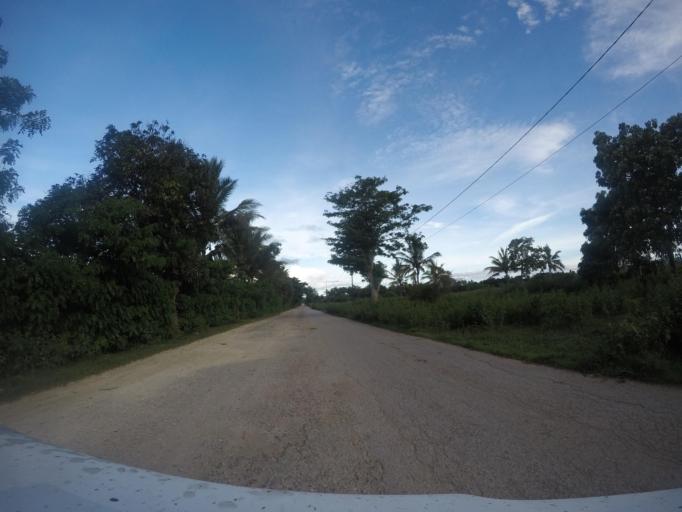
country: TL
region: Lautem
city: Lospalos
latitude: -8.5085
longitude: 126.9948
